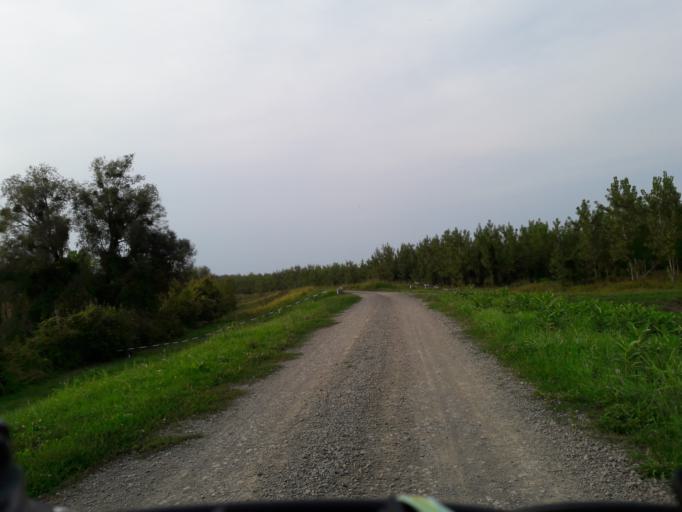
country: HR
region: Osjecko-Baranjska
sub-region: Grad Osijek
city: Osijek
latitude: 45.5745
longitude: 18.6686
